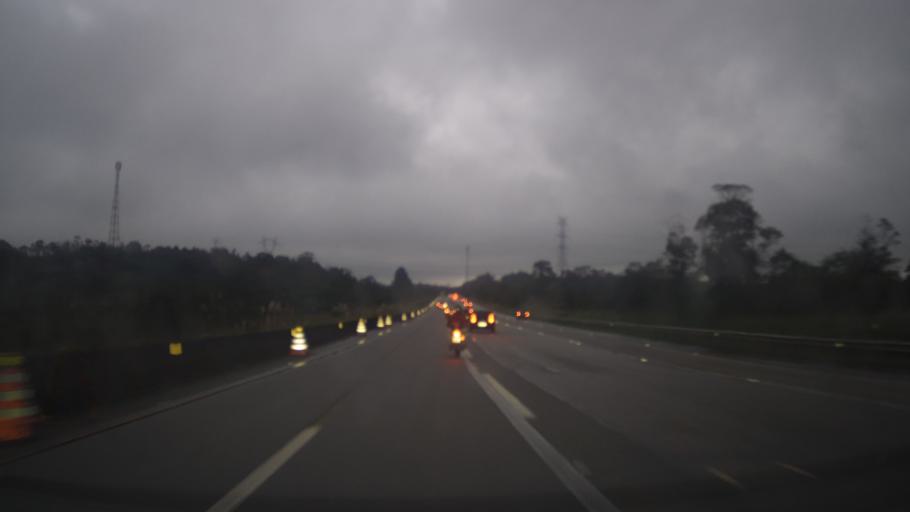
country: BR
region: Sao Paulo
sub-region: Cubatao
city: Cubatao
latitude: -23.8914
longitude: -46.5595
